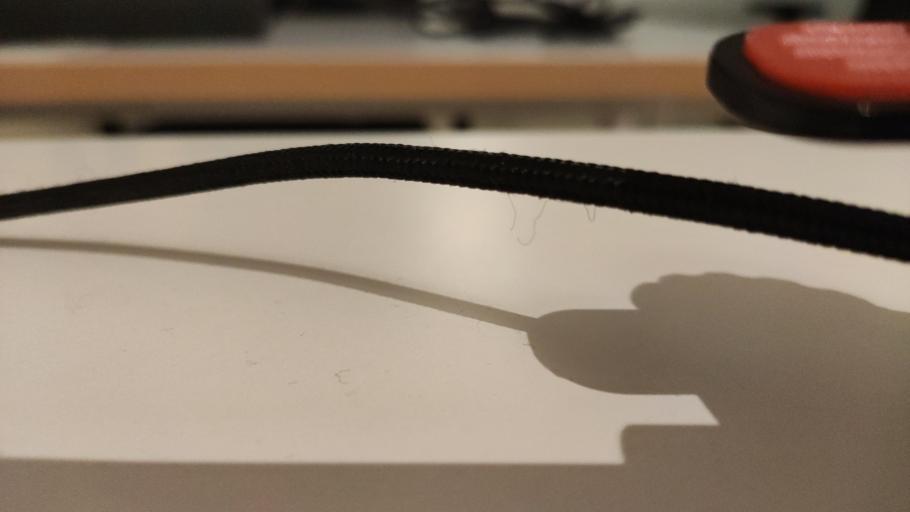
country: RU
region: Moskovskaya
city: Kurovskoye
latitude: 55.6028
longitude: 38.9264
